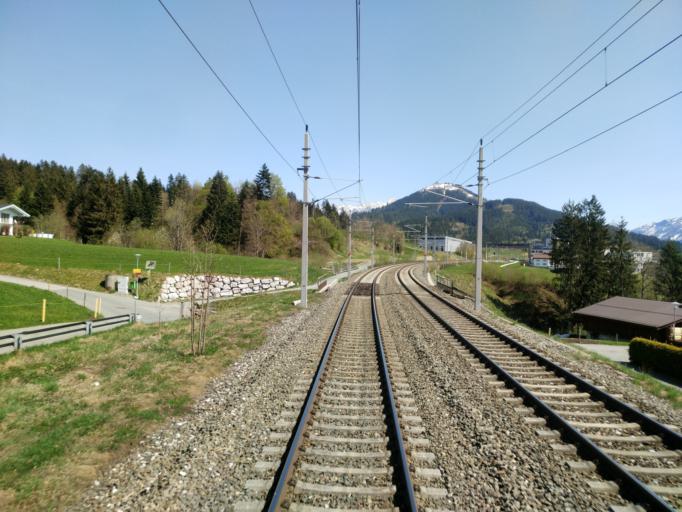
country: AT
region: Tyrol
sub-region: Politischer Bezirk Kitzbuhel
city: Fieberbrunn
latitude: 47.4928
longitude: 12.5224
